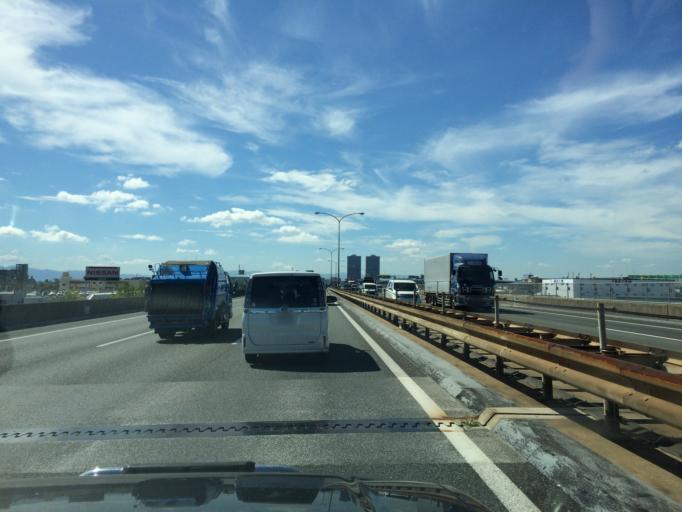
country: JP
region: Osaka
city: Yao
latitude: 34.6425
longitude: 135.5945
